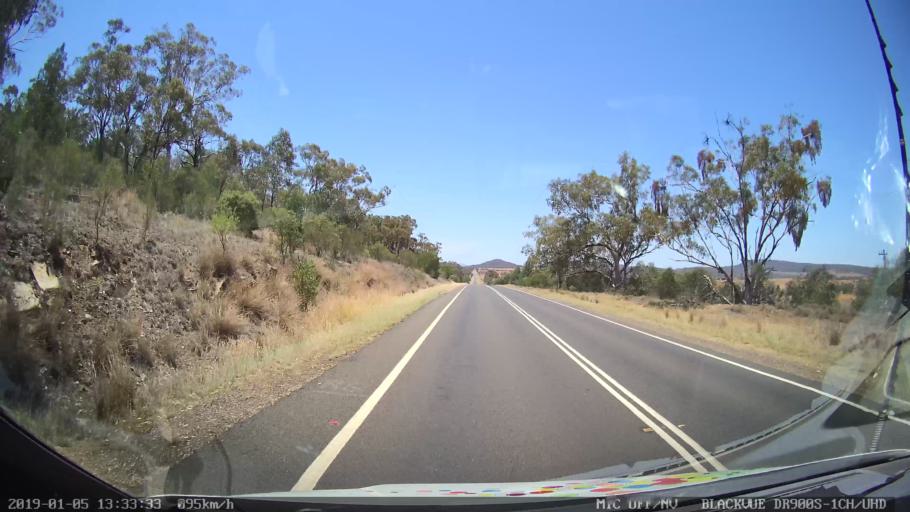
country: AU
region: New South Wales
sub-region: Gunnedah
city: Gunnedah
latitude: -31.0001
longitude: 150.1183
